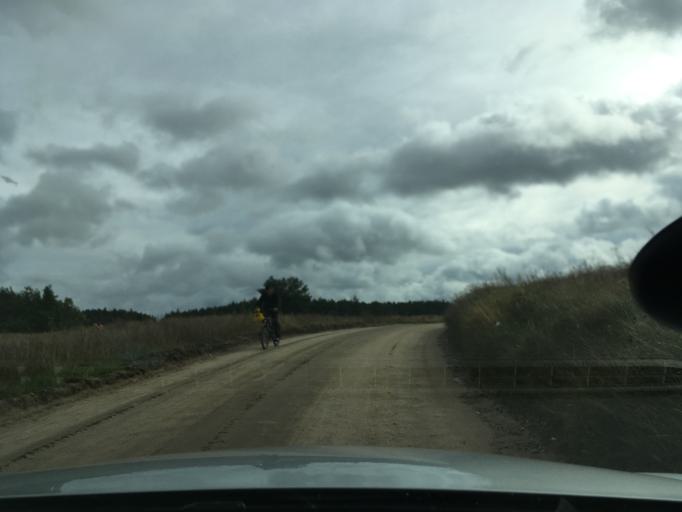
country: PL
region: Pomeranian Voivodeship
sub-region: Powiat koscierski
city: Koscierzyna
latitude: 54.1092
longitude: 18.0101
